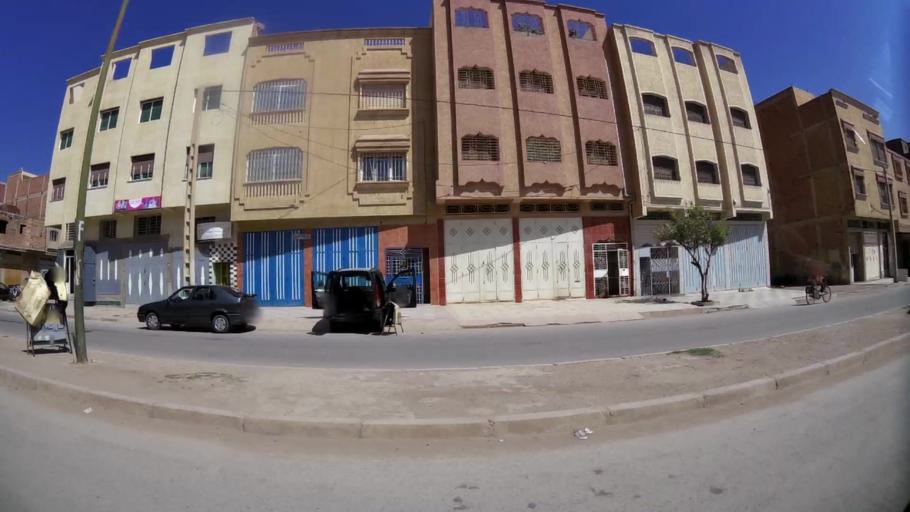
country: MA
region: Oriental
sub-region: Oujda-Angad
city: Oujda
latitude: 34.6699
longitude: -1.9453
